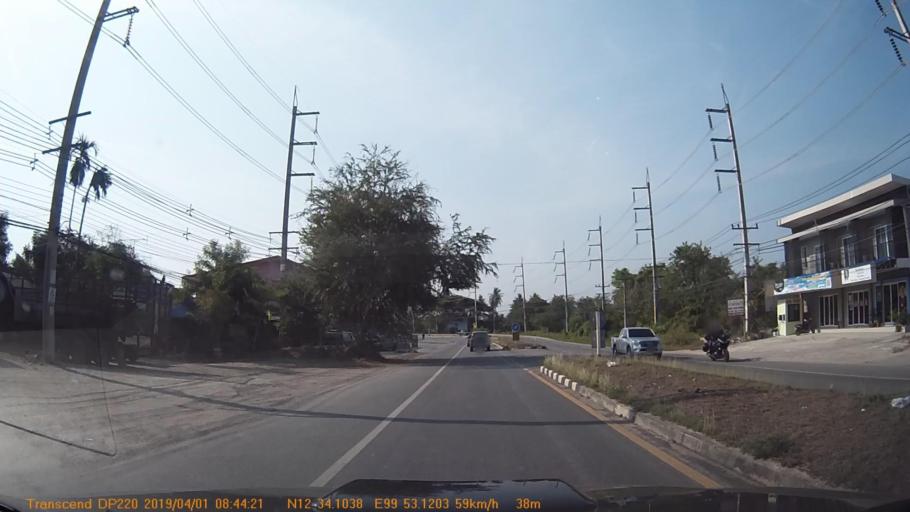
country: TH
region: Prachuap Khiri Khan
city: Hua Hin
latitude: 12.5684
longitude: 99.8853
